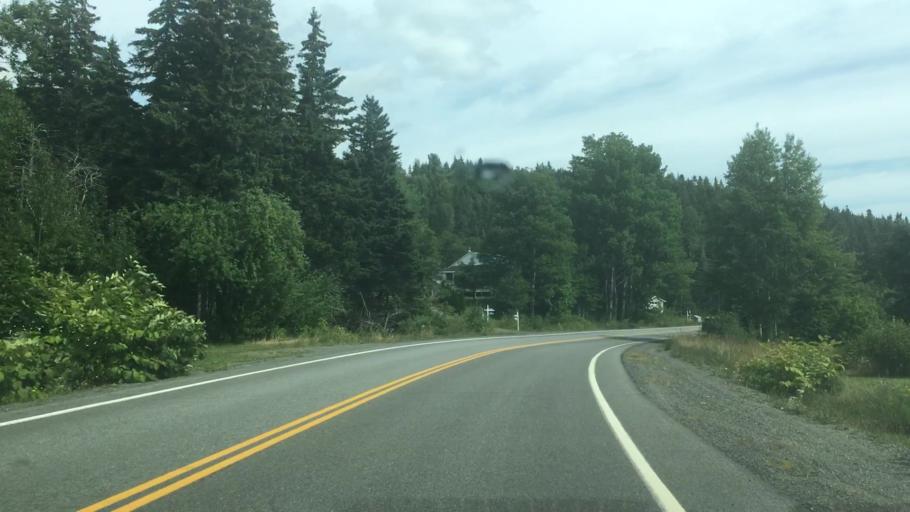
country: CA
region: Nova Scotia
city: Sydney Mines
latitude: 46.2660
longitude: -60.6208
